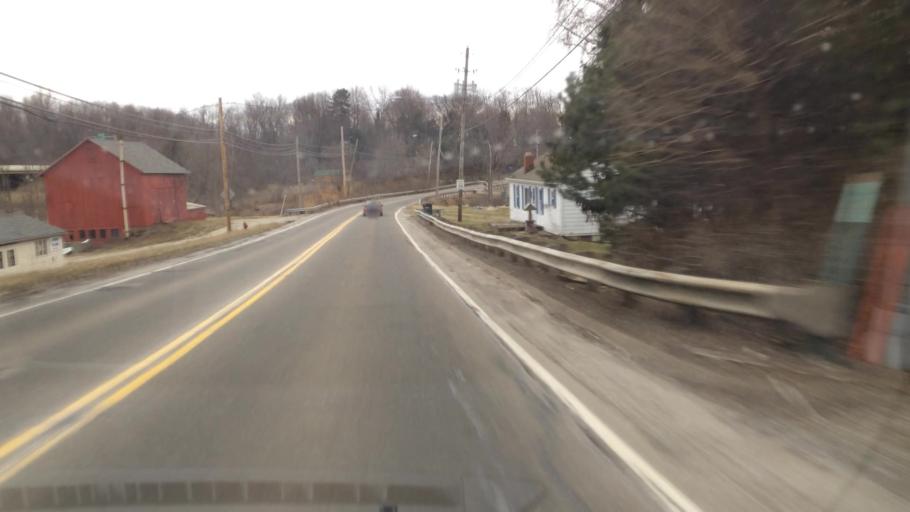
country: US
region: Ohio
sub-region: Summit County
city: Silver Lake
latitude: 41.1706
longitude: -81.4777
